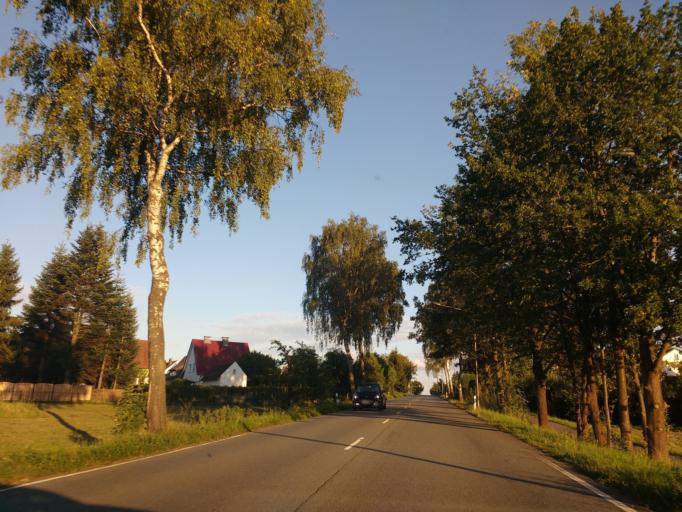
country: DE
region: North Rhine-Westphalia
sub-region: Regierungsbezirk Detmold
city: Detmold
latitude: 51.9816
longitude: 8.8910
